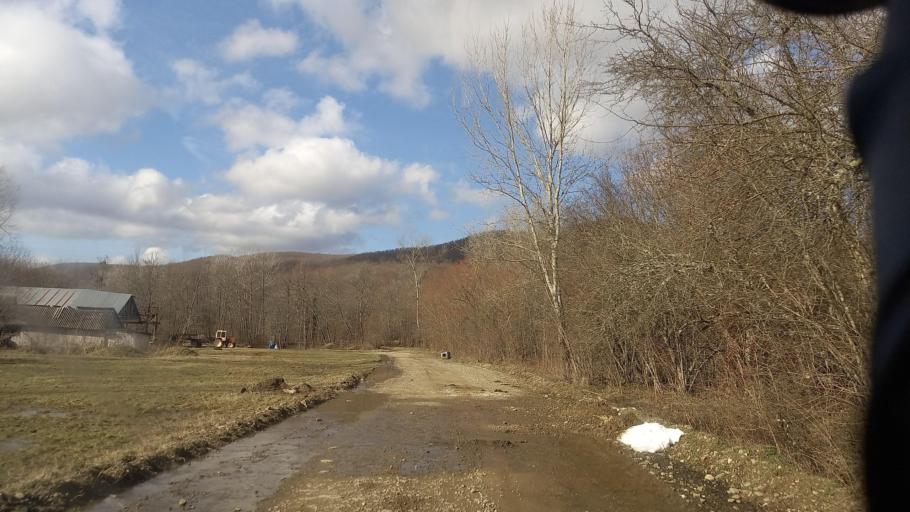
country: RU
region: Krasnodarskiy
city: Smolenskaya
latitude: 44.5984
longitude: 38.8803
